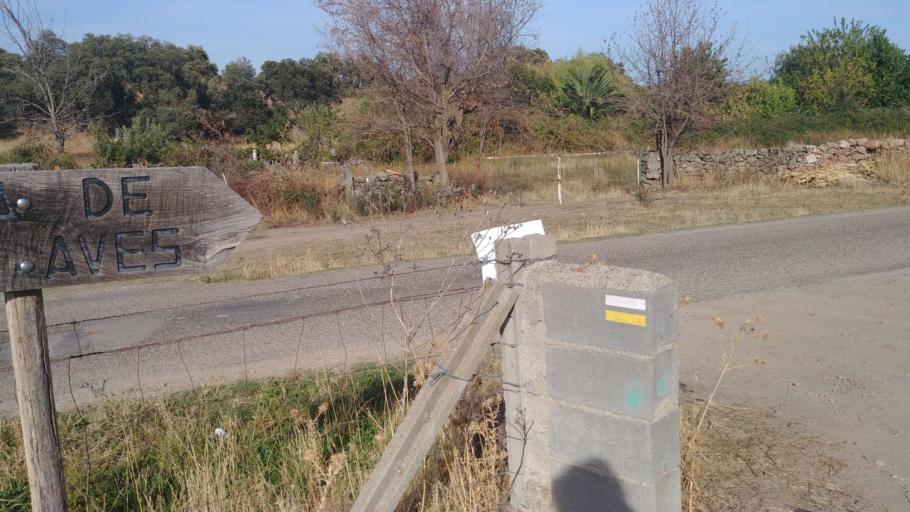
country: ES
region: Castille-La Mancha
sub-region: Province of Toledo
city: Navalcan
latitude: 40.0692
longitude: -5.1093
